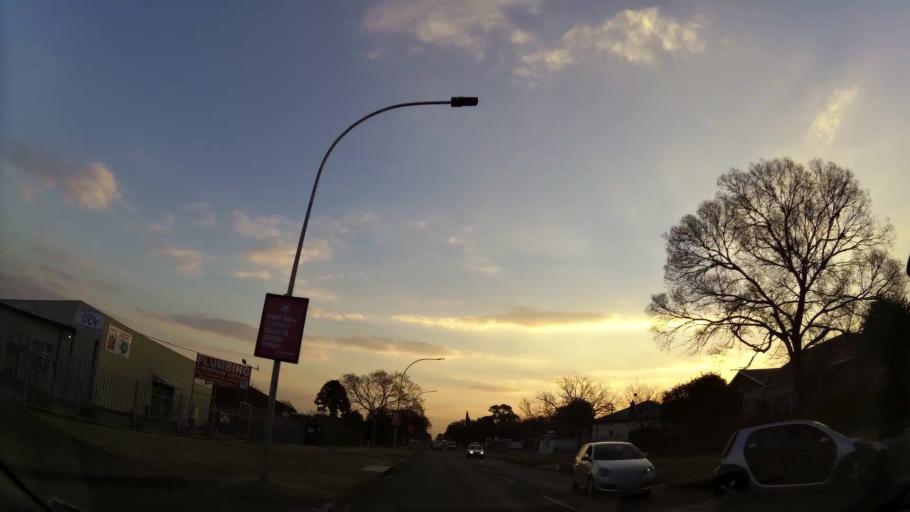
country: ZA
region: Gauteng
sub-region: Ekurhuleni Metropolitan Municipality
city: Benoni
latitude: -26.1749
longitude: 28.3283
